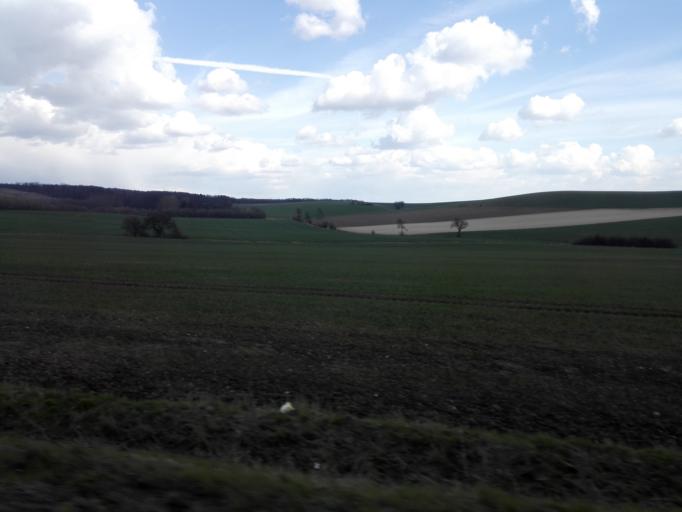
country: DE
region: Lower Saxony
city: Bad Salzdetfurth
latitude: 52.1134
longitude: 10.0475
